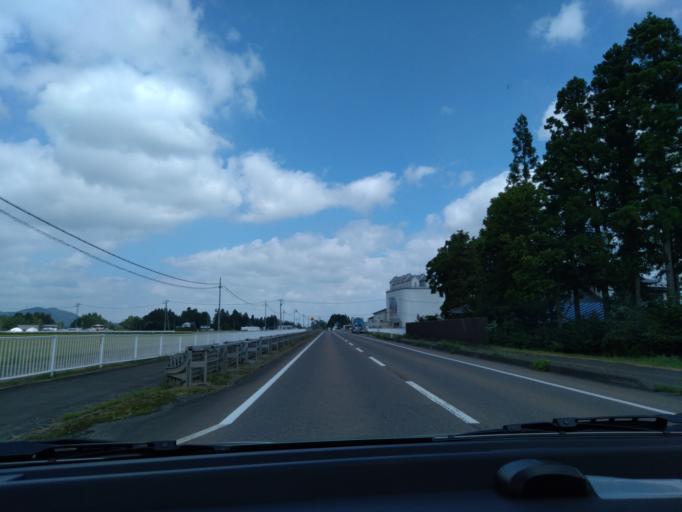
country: JP
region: Iwate
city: Hanamaki
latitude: 39.4046
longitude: 141.0689
